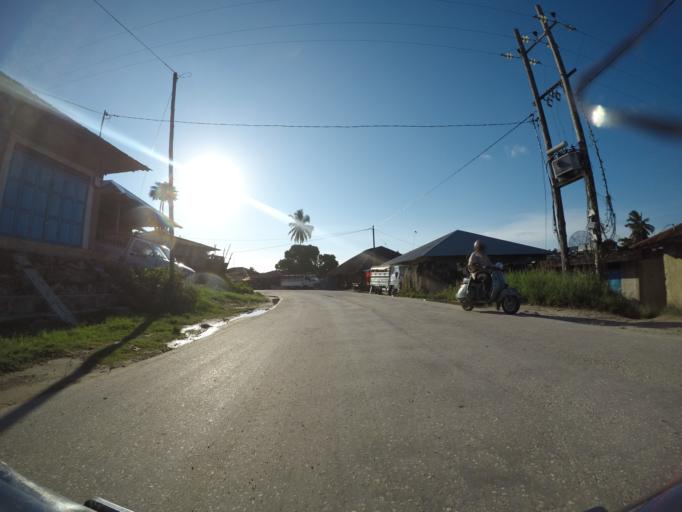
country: TZ
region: Pemba South
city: Mtambile
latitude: -5.3778
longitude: 39.7015
